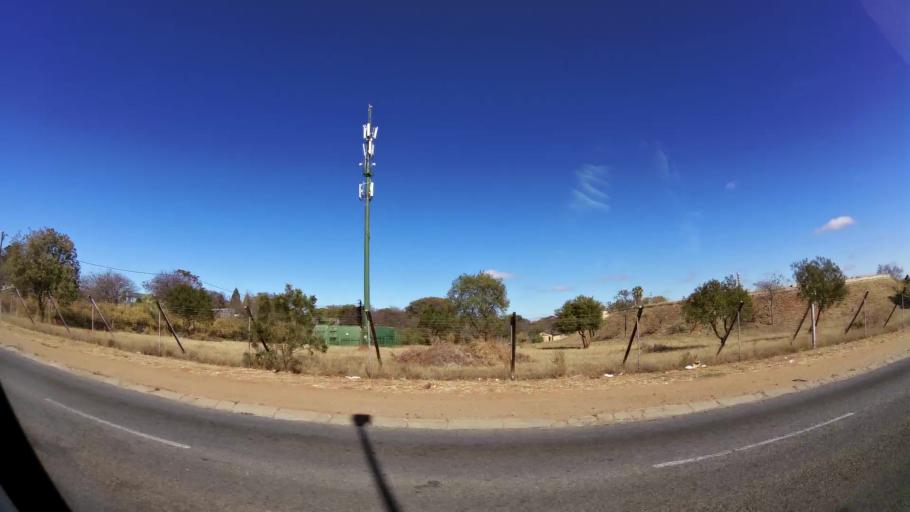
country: ZA
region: Limpopo
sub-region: Capricorn District Municipality
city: Polokwane
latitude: -23.8994
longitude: 29.4704
